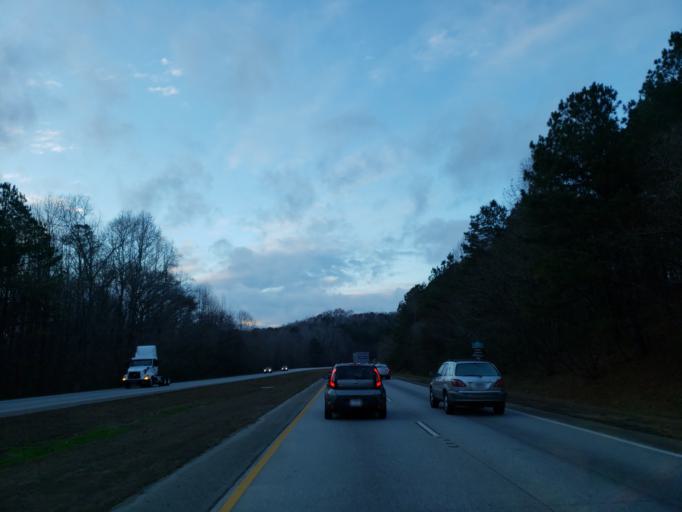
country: US
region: Georgia
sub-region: Fulton County
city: Union City
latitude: 33.6707
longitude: -84.5490
